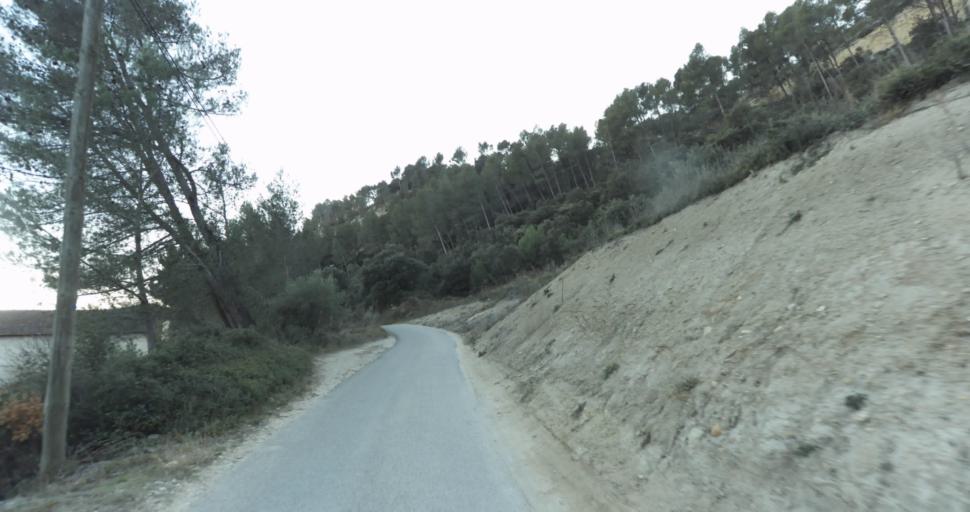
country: FR
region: Provence-Alpes-Cote d'Azur
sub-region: Departement des Bouches-du-Rhone
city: Barbentane
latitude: 43.8905
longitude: 4.7661
